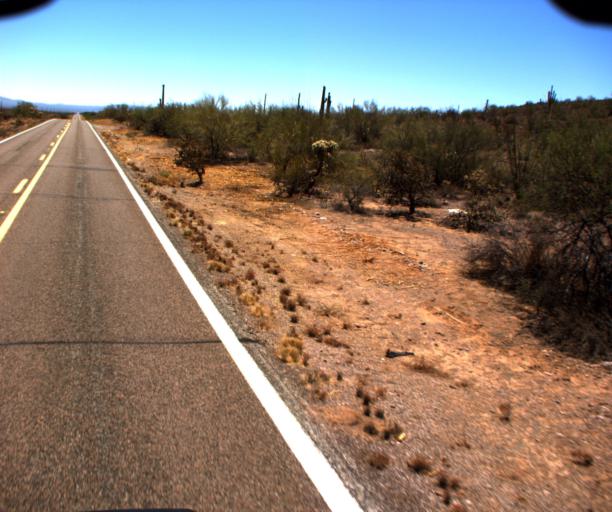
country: US
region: Arizona
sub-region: Pima County
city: Ajo
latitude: 32.2044
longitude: -112.5304
